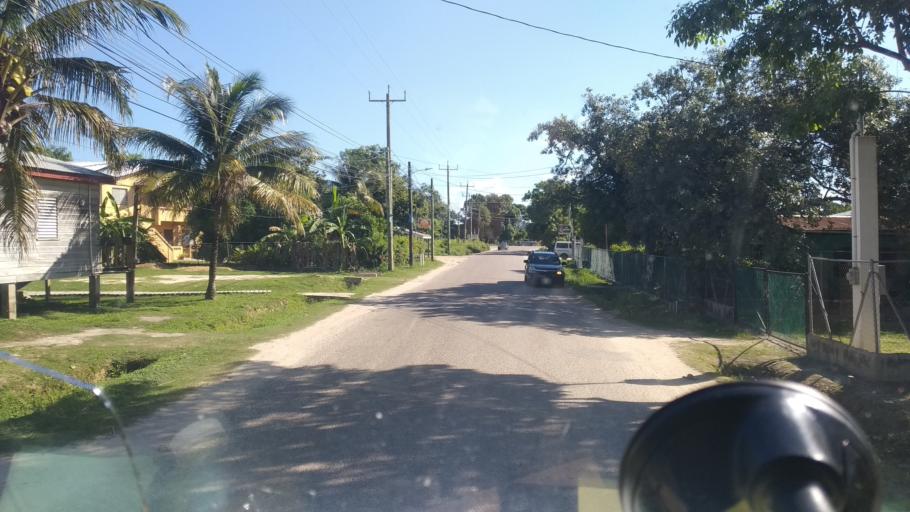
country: BZ
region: Belize
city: Belize City
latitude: 17.5549
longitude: -88.3103
